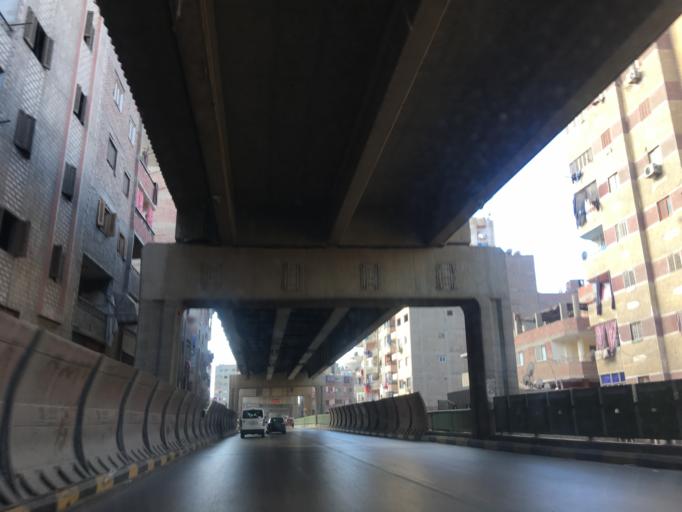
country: EG
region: Al Jizah
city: Al Jizah
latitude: 30.0298
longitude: 31.1784
